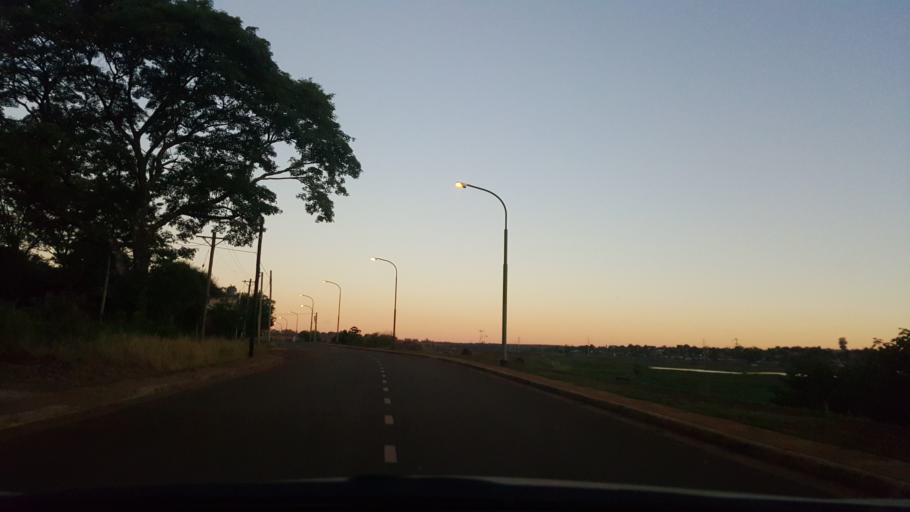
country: AR
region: Misiones
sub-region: Departamento de Capital
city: Posadas
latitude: -27.4235
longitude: -55.9044
